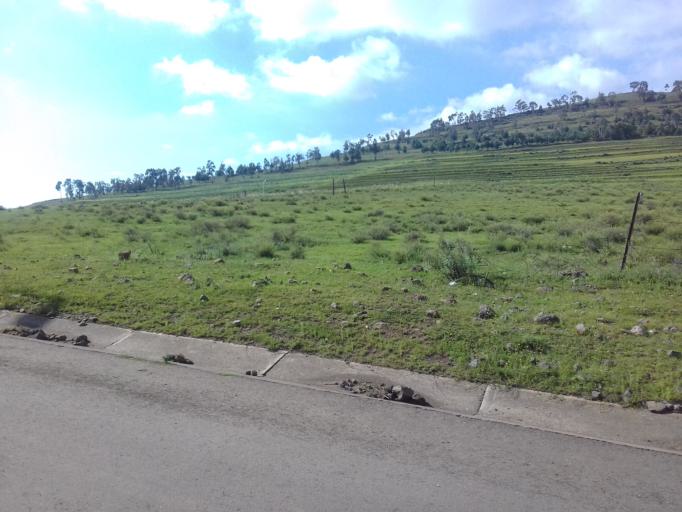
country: LS
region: Thaba-Tseka
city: Thaba-Tseka
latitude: -29.5240
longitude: 28.6121
